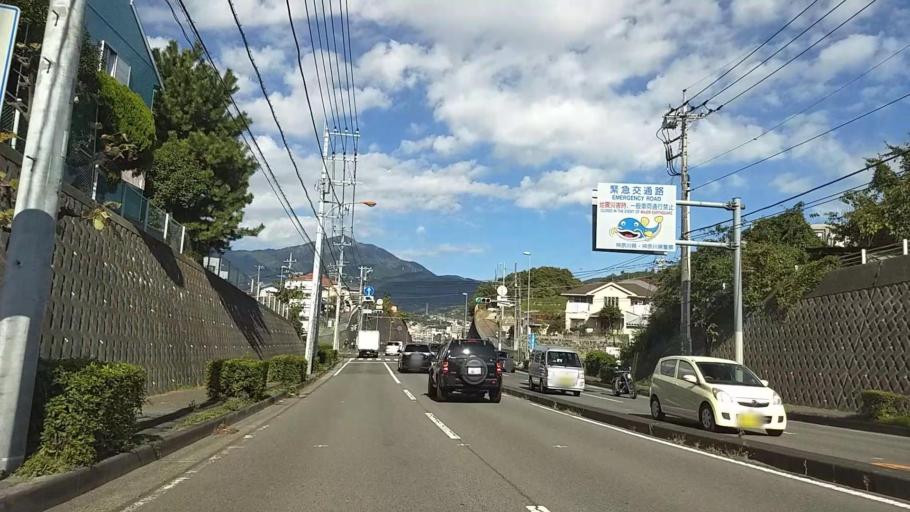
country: JP
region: Kanagawa
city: Hadano
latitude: 35.3629
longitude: 139.2339
